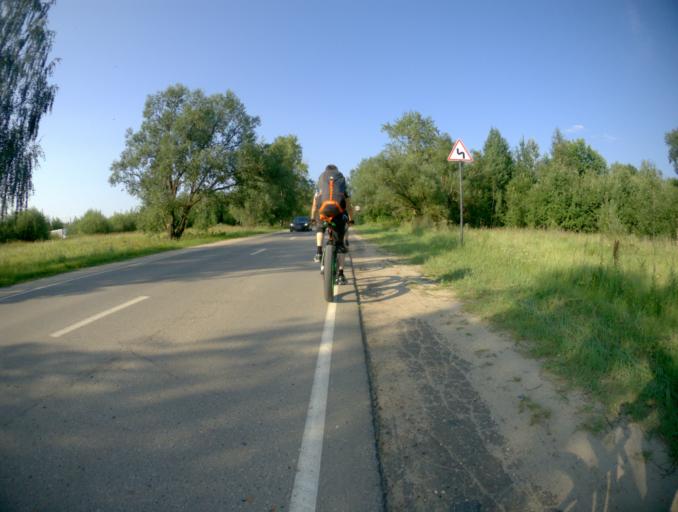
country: RU
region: Nizjnij Novgorod
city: Bor
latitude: 56.3494
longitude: 44.0518
